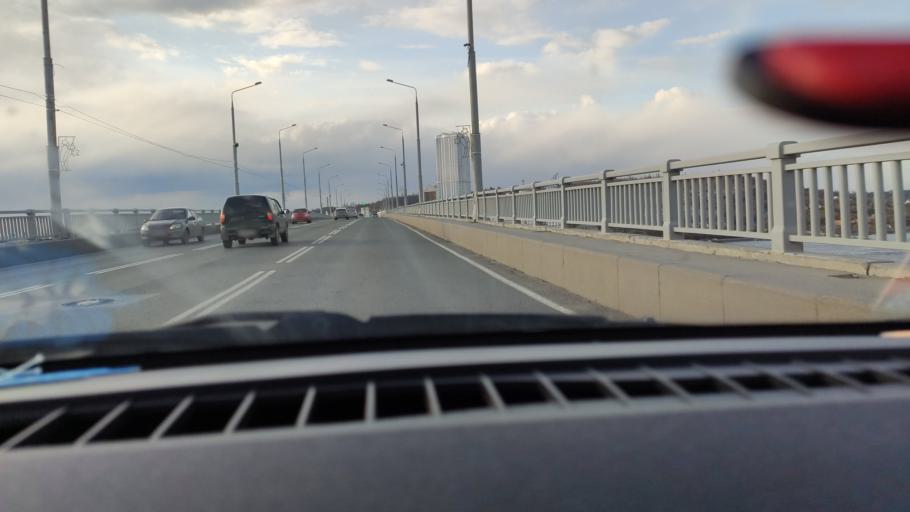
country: RU
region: Saratov
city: Engel's
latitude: 51.5256
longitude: 46.0655
